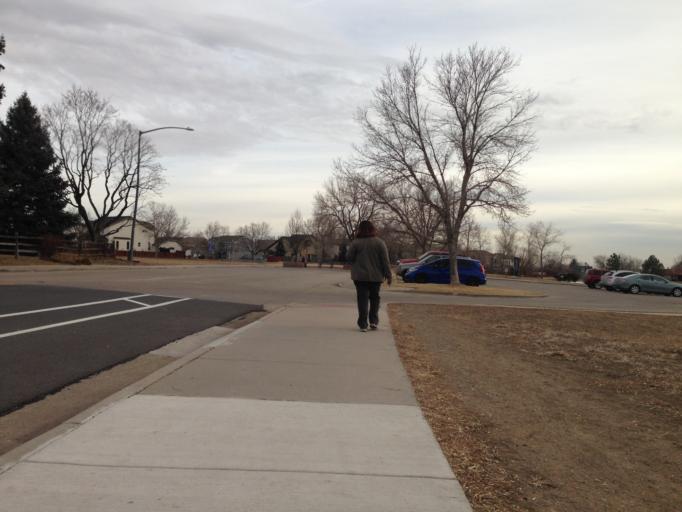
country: US
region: Colorado
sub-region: Adams County
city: Westminster
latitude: 39.8443
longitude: -105.0640
